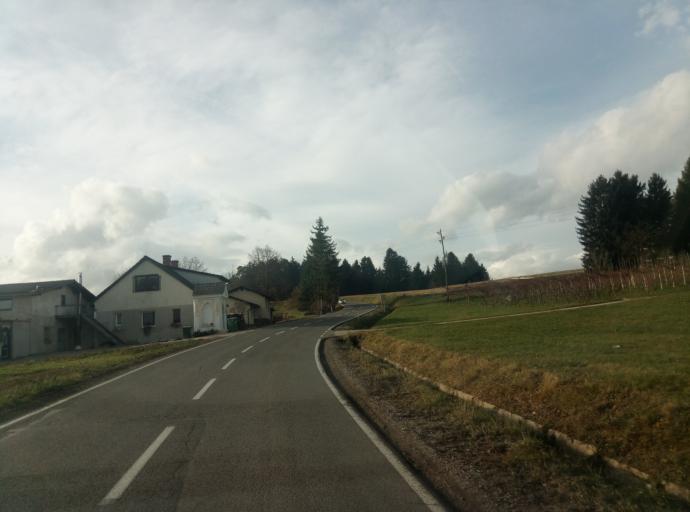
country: SI
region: Sentjur pri Celju
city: Sentjur
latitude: 46.2384
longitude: 15.3800
